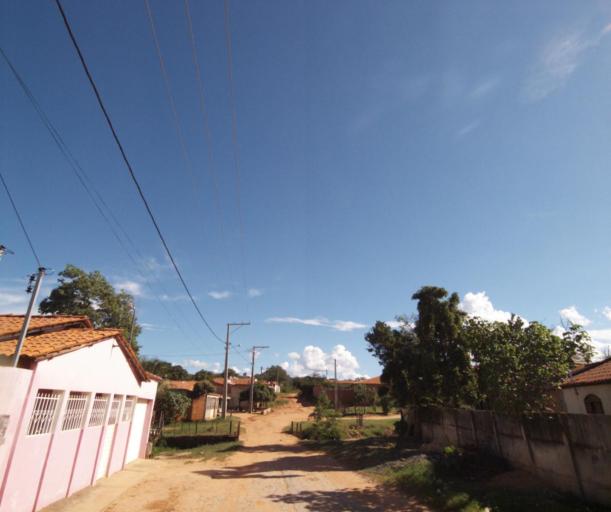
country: BR
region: Bahia
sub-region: Correntina
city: Correntina
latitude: -13.3478
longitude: -44.6343
